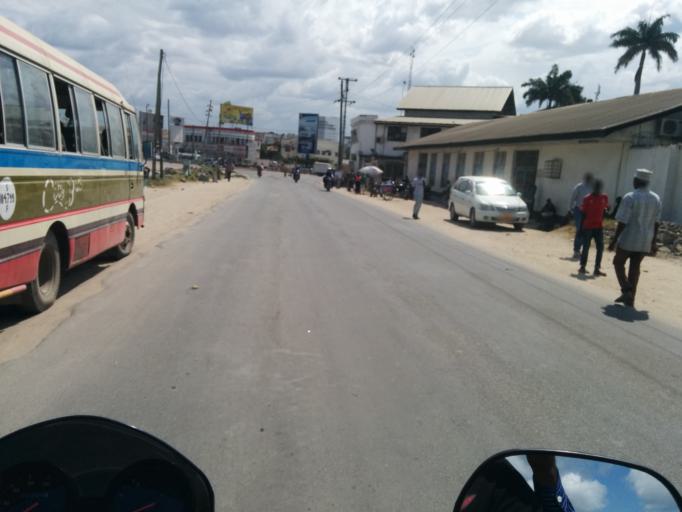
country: TZ
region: Dar es Salaam
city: Dar es Salaam
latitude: -6.8282
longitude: 39.2771
